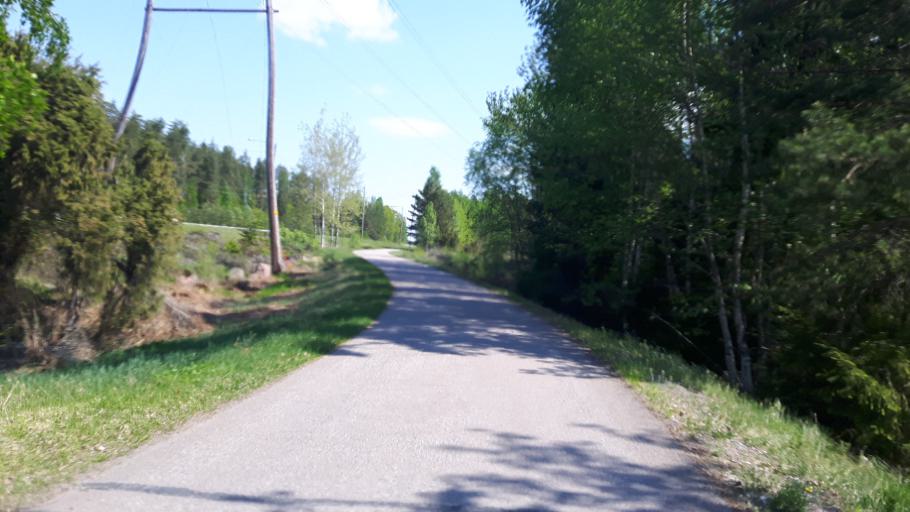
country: FI
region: Uusimaa
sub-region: Loviisa
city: Lovisa
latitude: 60.4674
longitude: 26.2786
